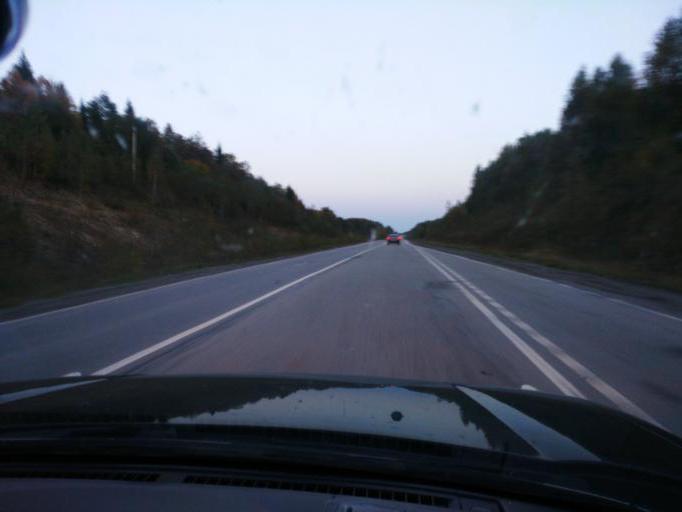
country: RU
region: Perm
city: Verkhnechusovskiye Gorodki
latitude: 58.2760
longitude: 56.9361
